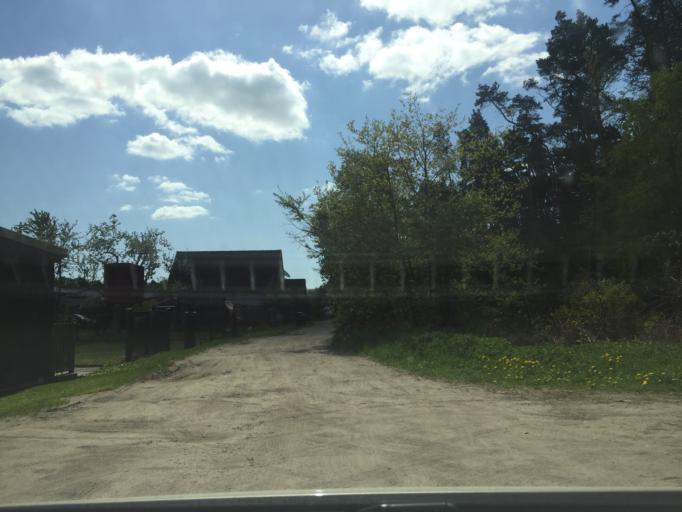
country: DE
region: Mecklenburg-Vorpommern
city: Torgelow
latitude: 53.6247
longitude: 13.9887
